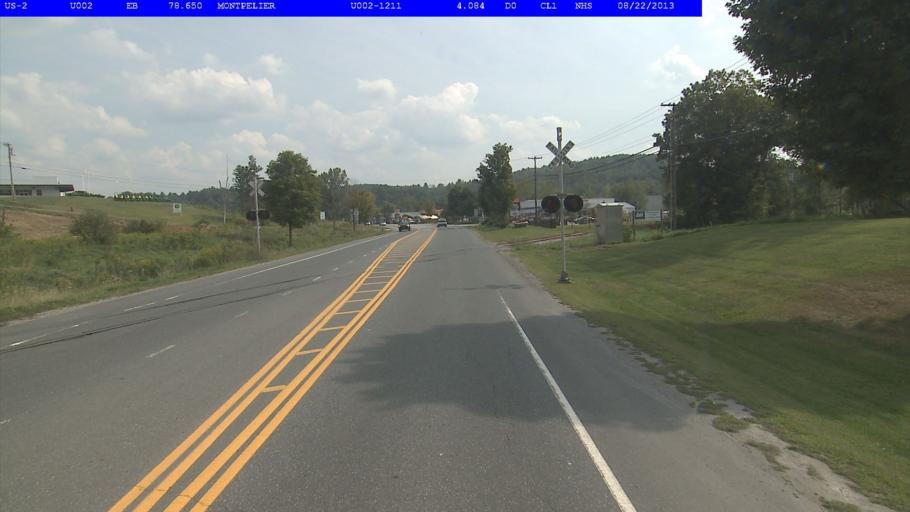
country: US
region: Vermont
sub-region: Washington County
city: Montpelier
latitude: 44.2449
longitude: -72.5479
